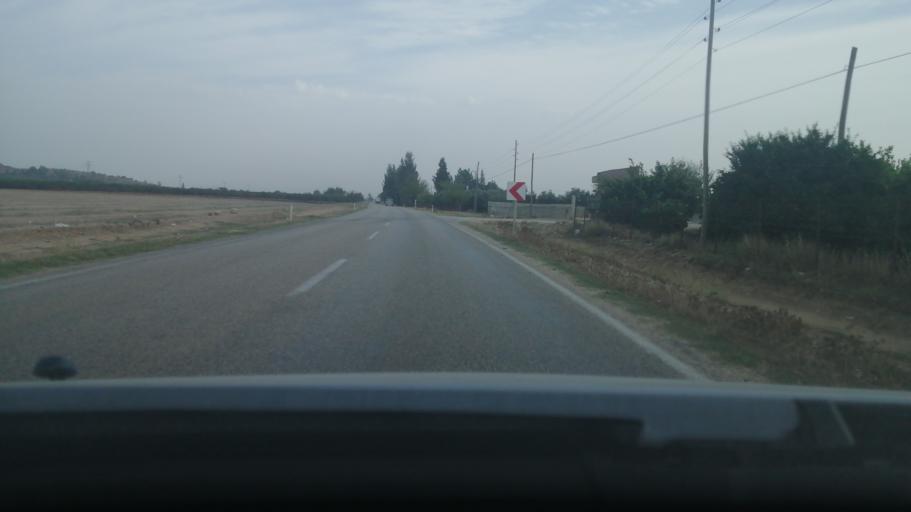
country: TR
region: Adana
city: Kozan
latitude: 37.3761
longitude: 35.8330
